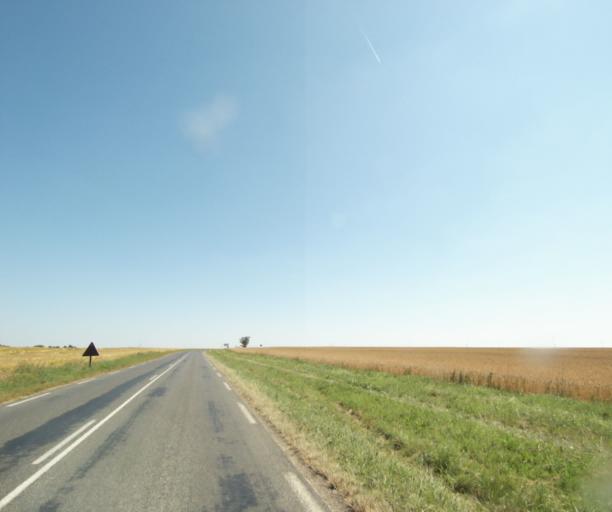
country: FR
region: Ile-de-France
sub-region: Departement de Seine-et-Marne
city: La Chapelle-la-Reine
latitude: 48.2884
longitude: 2.5789
